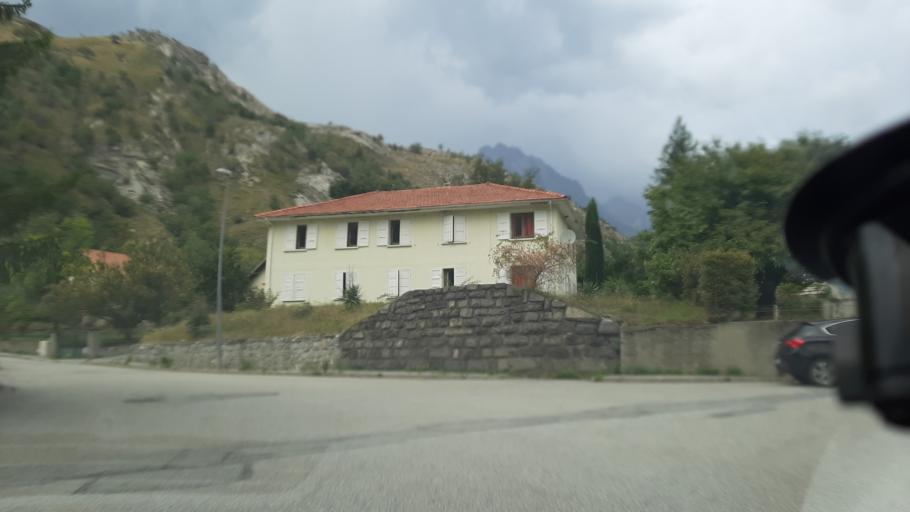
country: FR
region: Rhone-Alpes
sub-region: Departement de la Savoie
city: Saint-Michel-de-Maurienne
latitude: 45.2228
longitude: 6.4598
